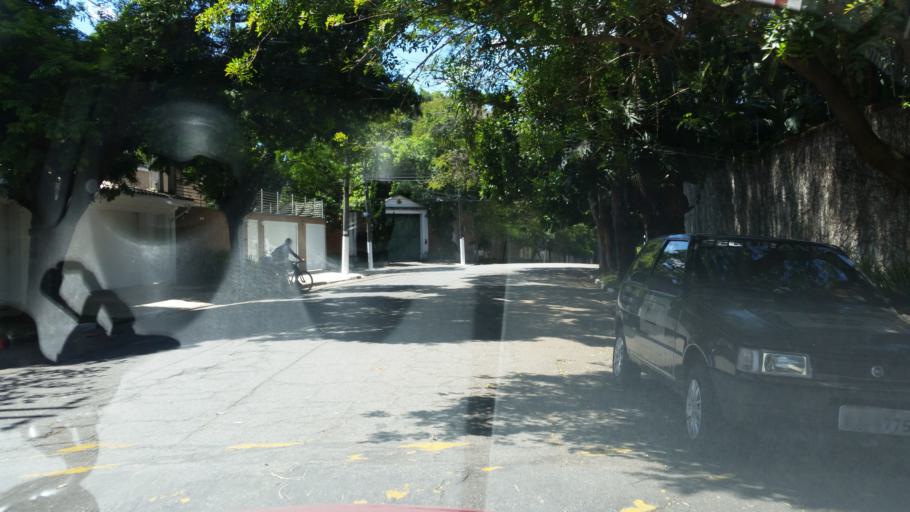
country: BR
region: Sao Paulo
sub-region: Diadema
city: Diadema
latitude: -23.6431
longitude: -46.6882
